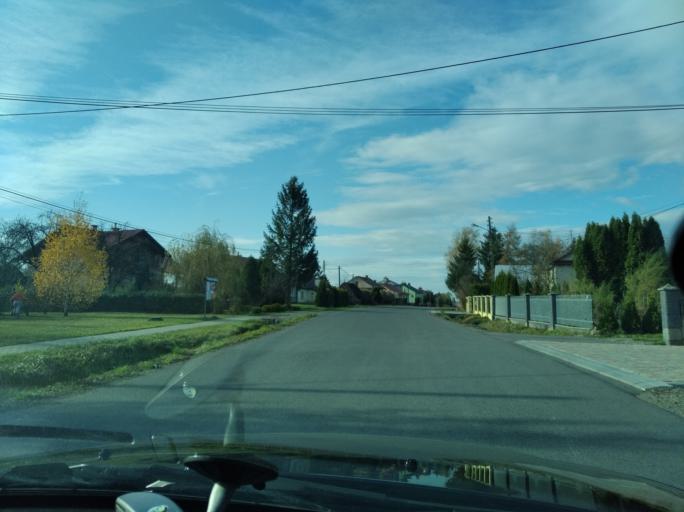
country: PL
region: Subcarpathian Voivodeship
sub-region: Powiat ropczycko-sedziszowski
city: Sedziszow Malopolski
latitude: 50.0809
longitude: 21.7281
